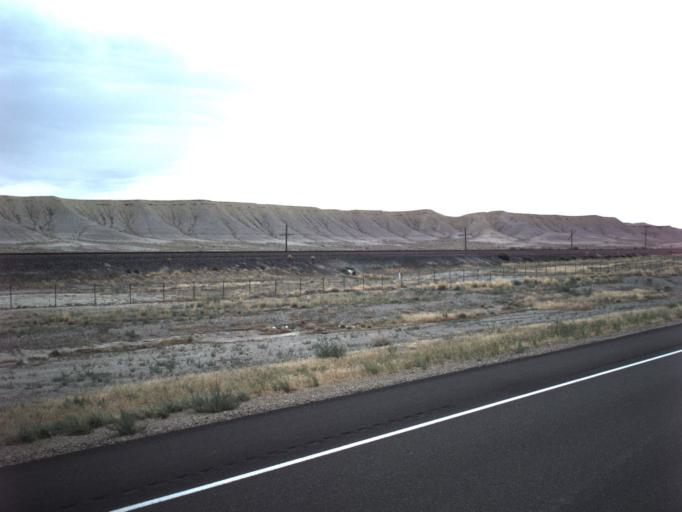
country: US
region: Utah
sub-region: Carbon County
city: East Carbon City
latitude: 39.0465
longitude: -110.3092
